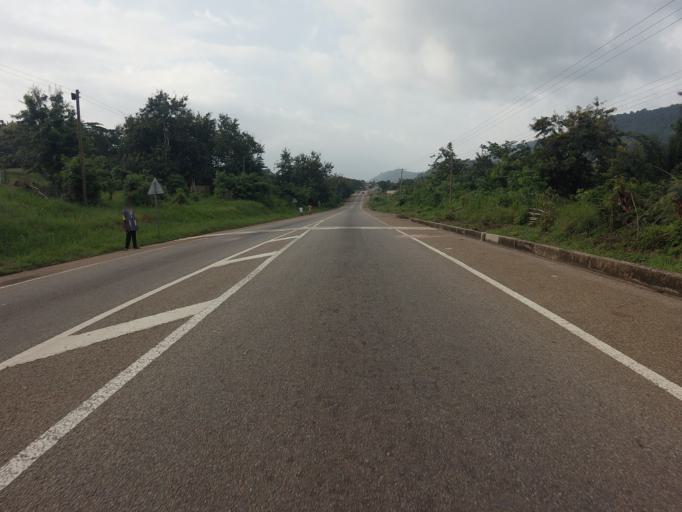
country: GH
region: Volta
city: Ho
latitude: 6.6619
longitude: 0.4723
